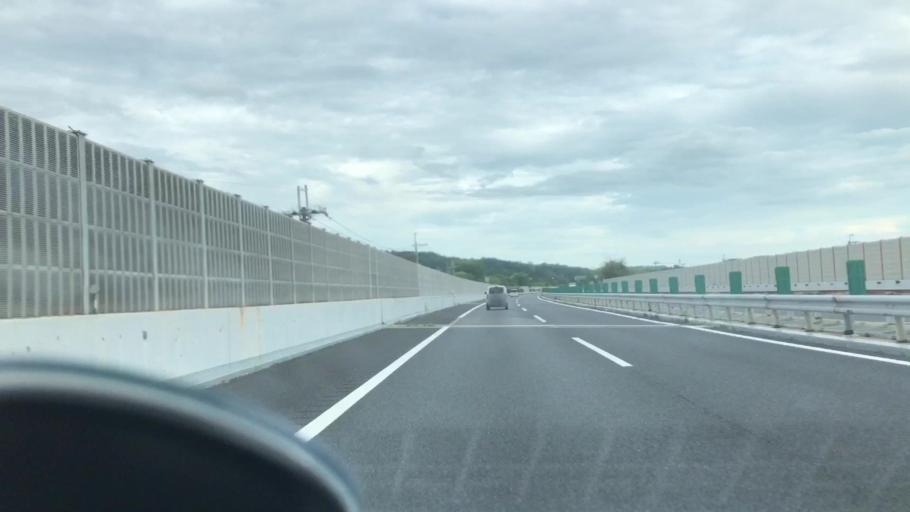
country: JP
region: Hyogo
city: Yashiro
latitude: 34.9278
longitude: 134.9836
